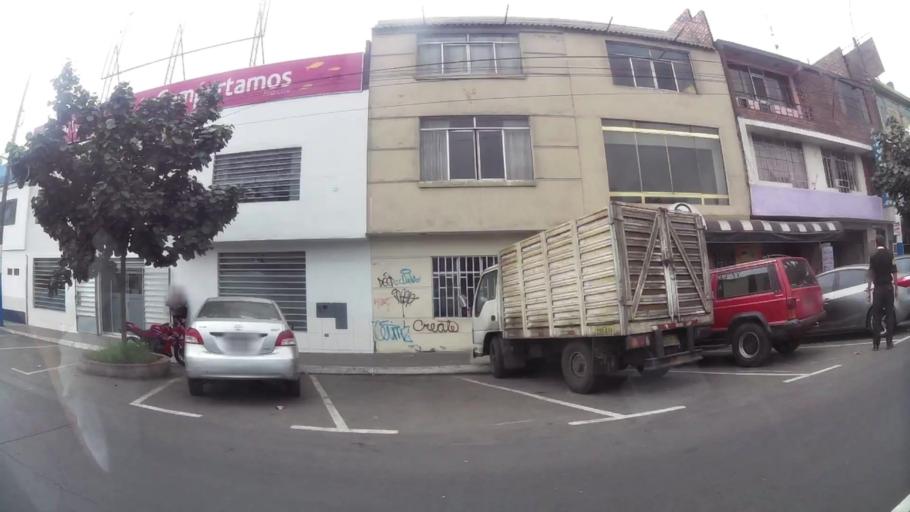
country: PE
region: Callao
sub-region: Callao
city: Callao
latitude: -12.0311
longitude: -77.0824
